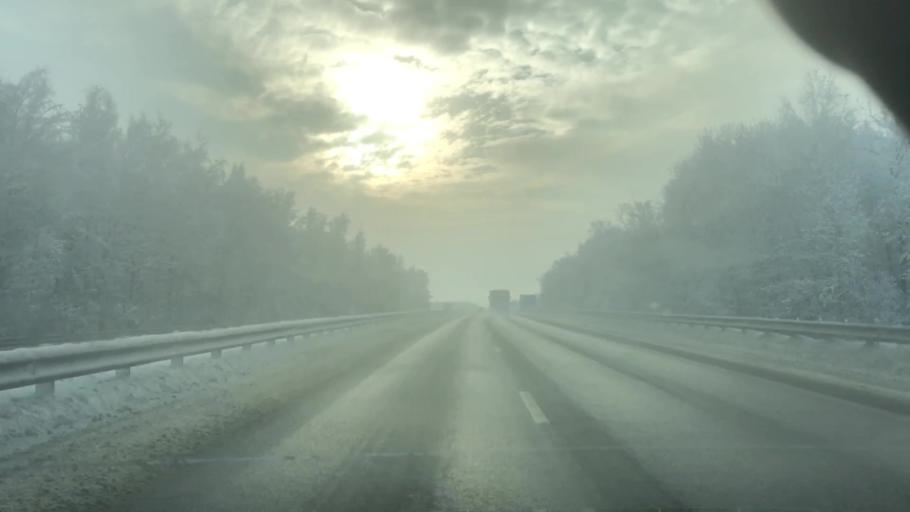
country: RU
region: Tula
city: Venev
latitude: 54.3812
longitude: 38.1551
